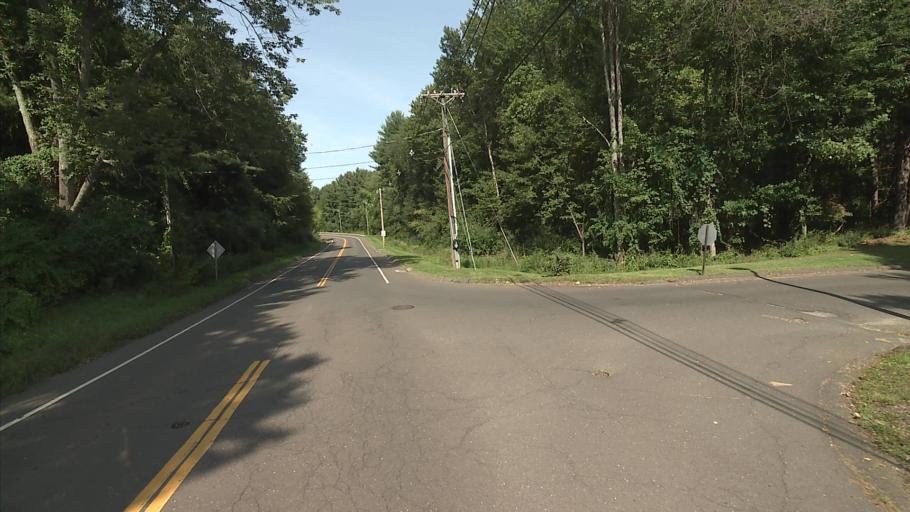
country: US
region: Connecticut
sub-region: Fairfield County
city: Newtown
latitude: 41.3985
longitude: -73.2748
